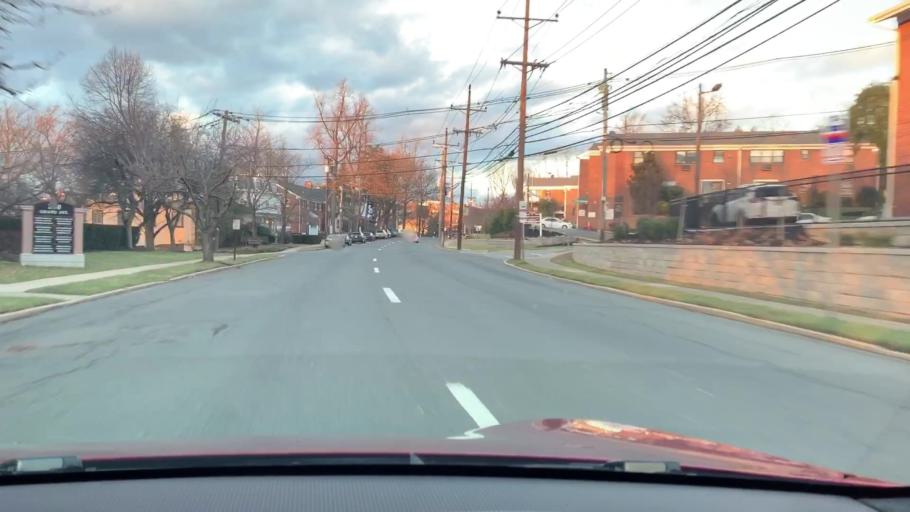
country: US
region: New Jersey
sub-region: Bergen County
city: Englewood
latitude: 40.8866
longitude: -73.9774
